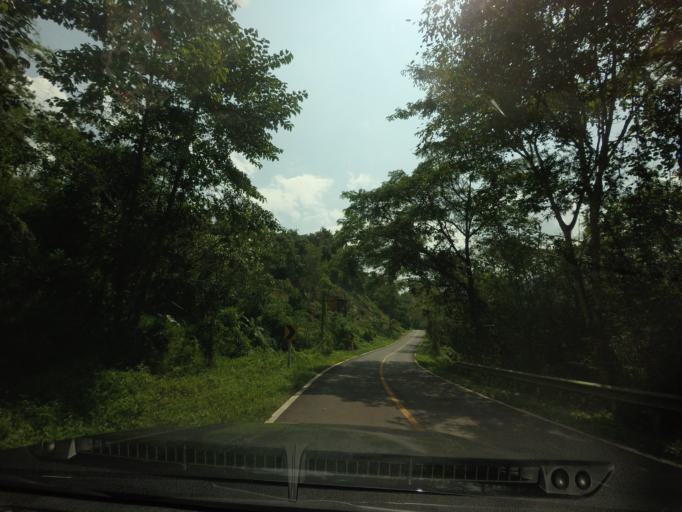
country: TH
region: Nan
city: Bo Kluea
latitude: 19.1577
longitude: 101.1594
